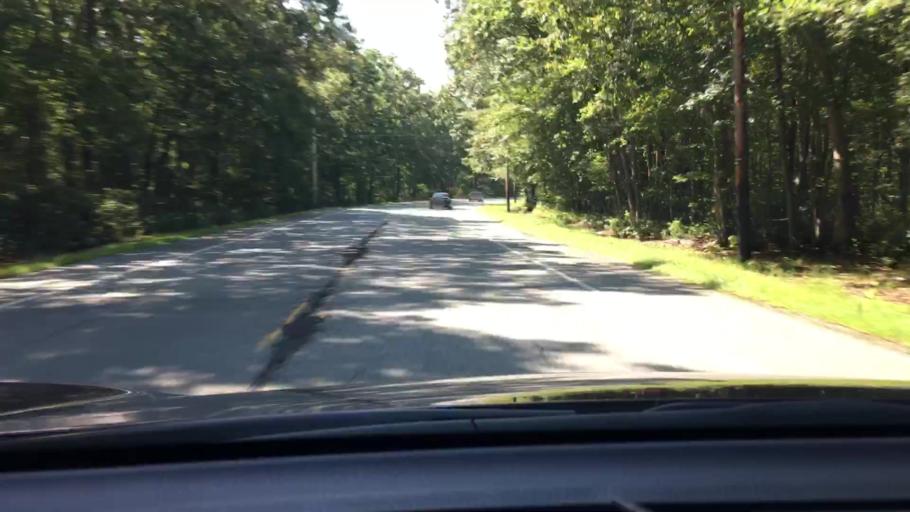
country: US
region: New Jersey
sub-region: Cape May County
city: Woodbine
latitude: 39.2533
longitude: -74.8060
